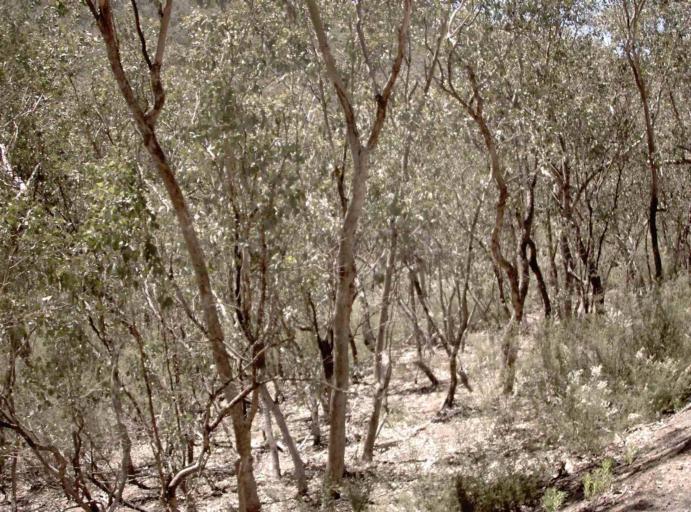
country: AU
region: New South Wales
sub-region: Snowy River
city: Jindabyne
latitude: -37.0701
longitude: 148.4979
